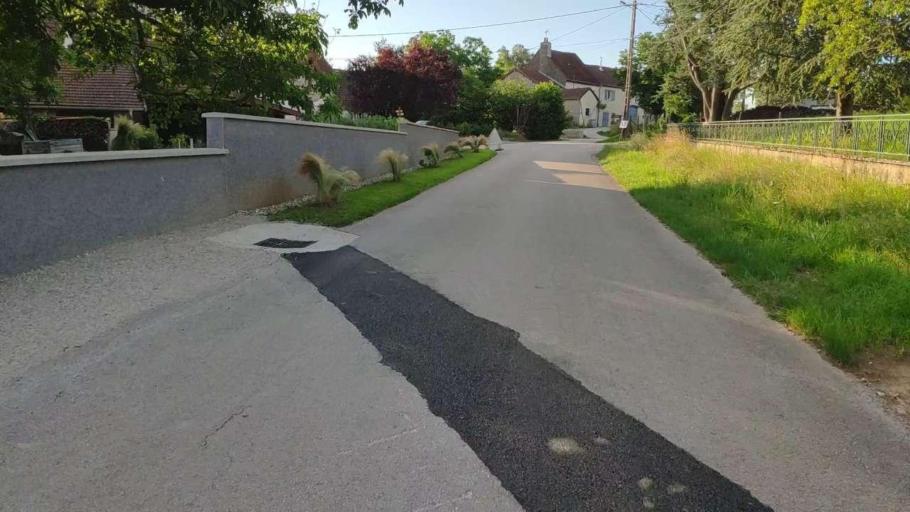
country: FR
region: Franche-Comte
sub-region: Departement du Jura
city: Bletterans
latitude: 46.7802
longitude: 5.4932
